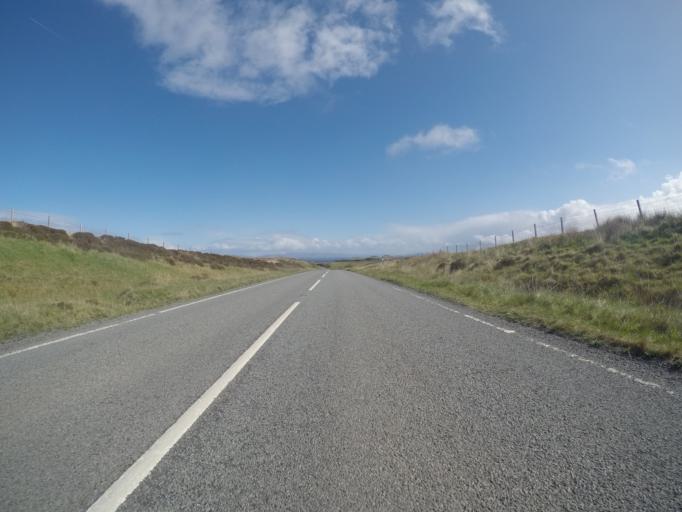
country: GB
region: Scotland
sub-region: Highland
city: Portree
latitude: 57.6180
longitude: -6.1934
